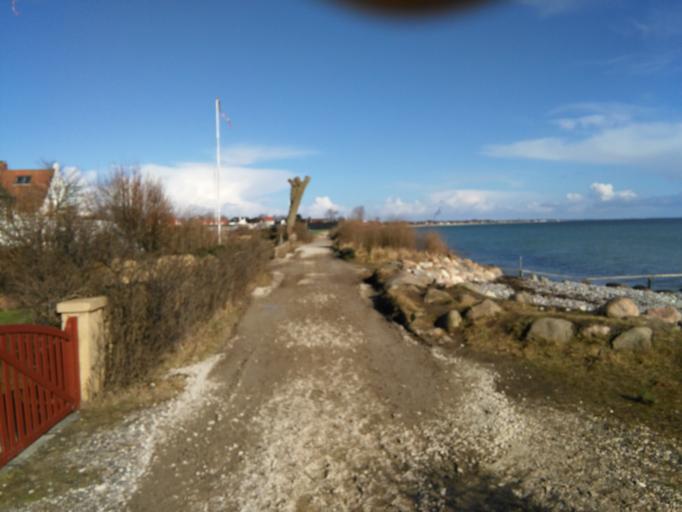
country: DK
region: Central Jutland
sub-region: Arhus Kommune
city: Arhus
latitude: 56.1824
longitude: 10.2367
